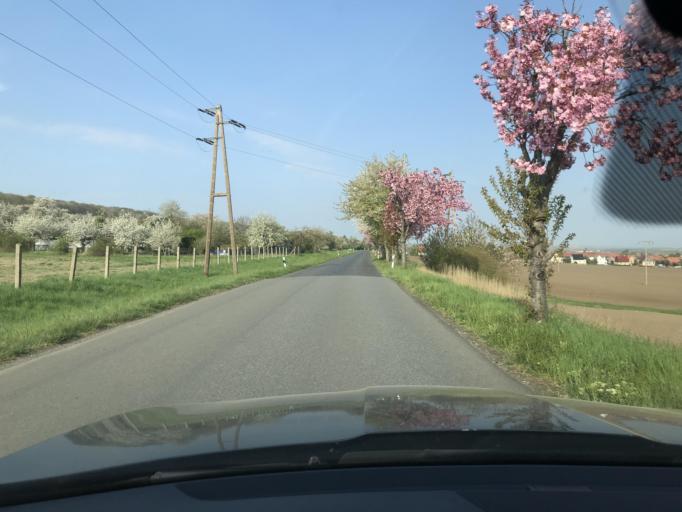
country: DE
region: Saxony-Anhalt
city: Strobeck
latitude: 51.9741
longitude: 10.9930
